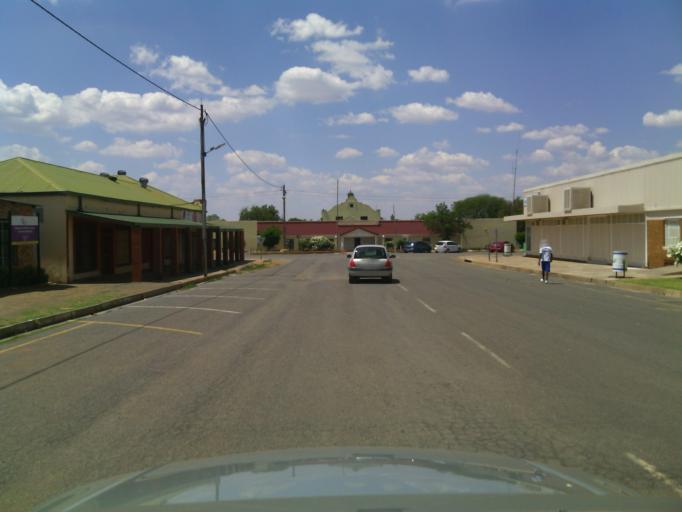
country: ZA
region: Orange Free State
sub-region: Xhariep District Municipality
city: Dewetsdorp
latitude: -29.5842
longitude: 26.6631
